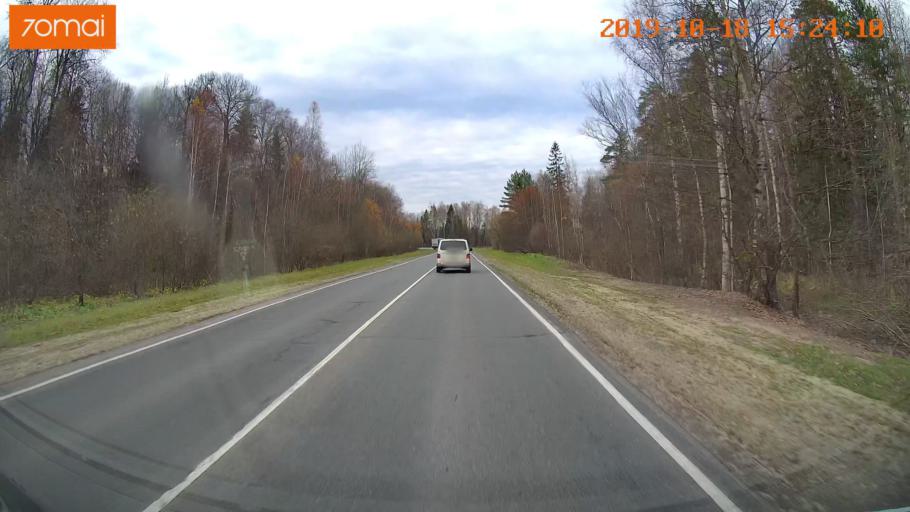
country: RU
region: Vladimir
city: Anopino
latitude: 55.7311
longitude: 40.7250
